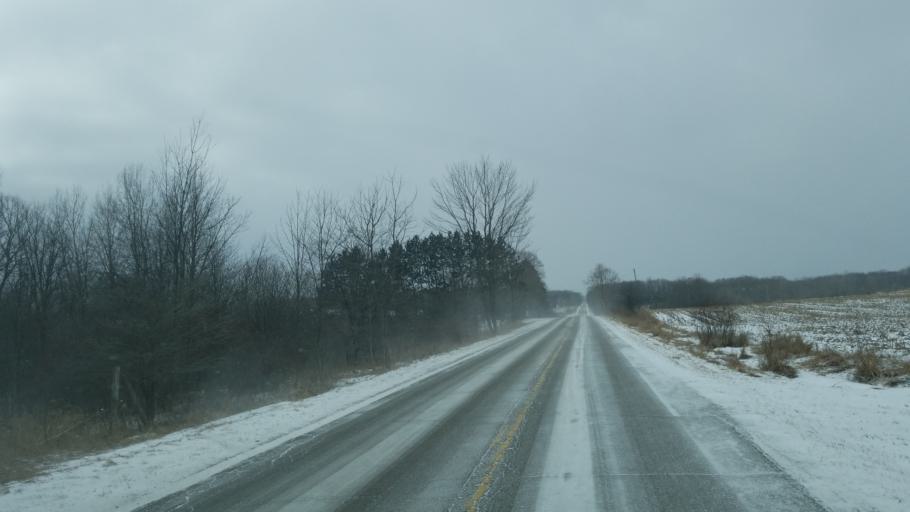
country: US
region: Michigan
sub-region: Osceola County
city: Evart
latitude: 44.0303
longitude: -85.2216
